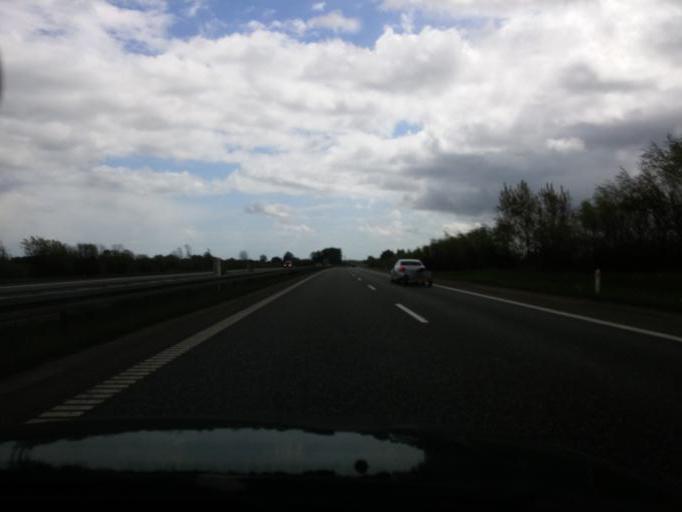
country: DK
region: South Denmark
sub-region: Faaborg-Midtfyn Kommune
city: Ringe
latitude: 55.2695
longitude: 10.4654
